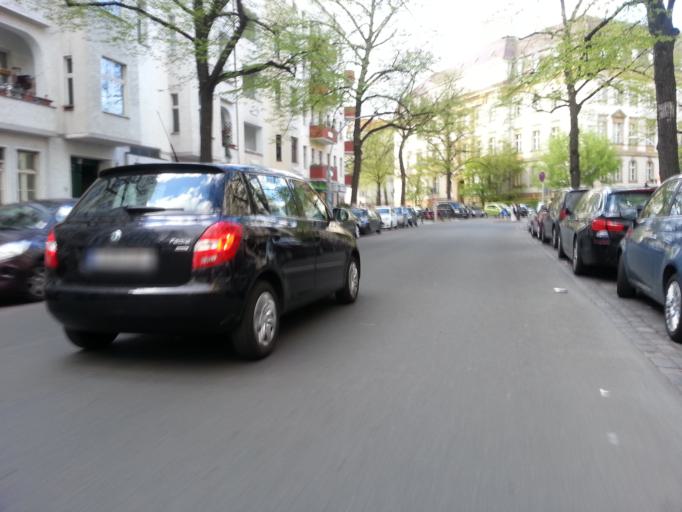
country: DE
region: Berlin
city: Halensee
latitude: 52.5044
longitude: 13.2949
